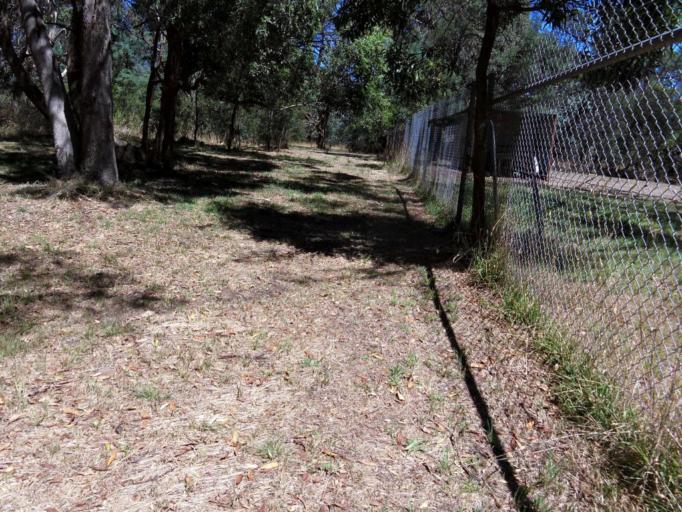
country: AU
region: Victoria
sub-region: Hume
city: Sunbury
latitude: -37.3583
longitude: 144.5487
